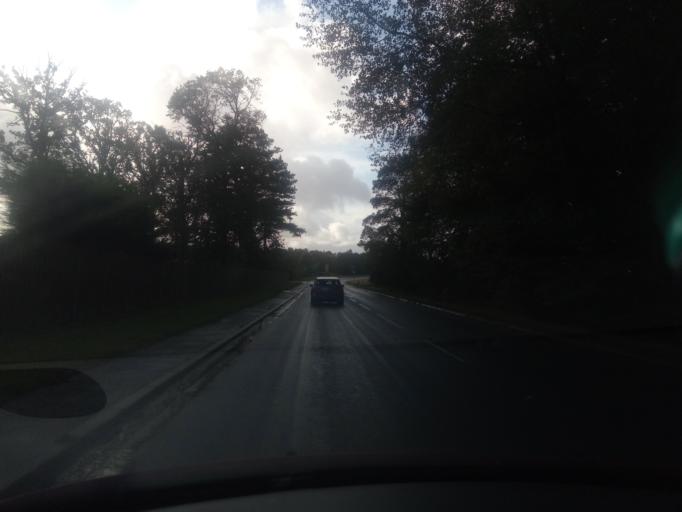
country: GB
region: England
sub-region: Cumbria
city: Carlisle
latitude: 54.9348
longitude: -2.9453
